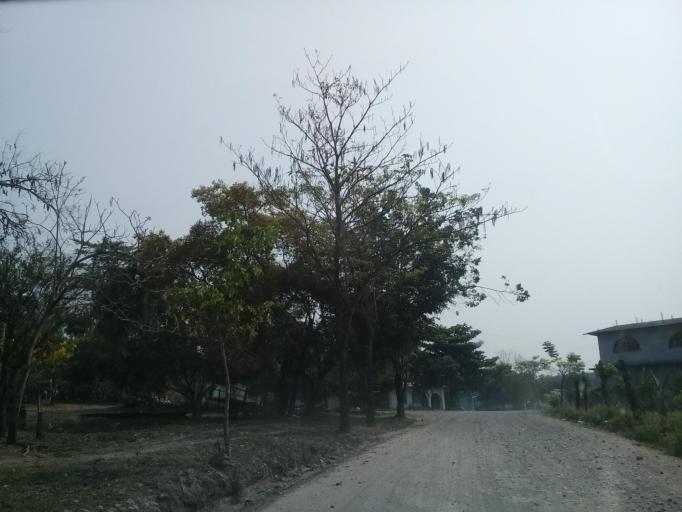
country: MX
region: Oaxaca
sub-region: Acatlan de Perez Figueroa
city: Zona Urbana Ejidal
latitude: 18.5886
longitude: -96.5614
